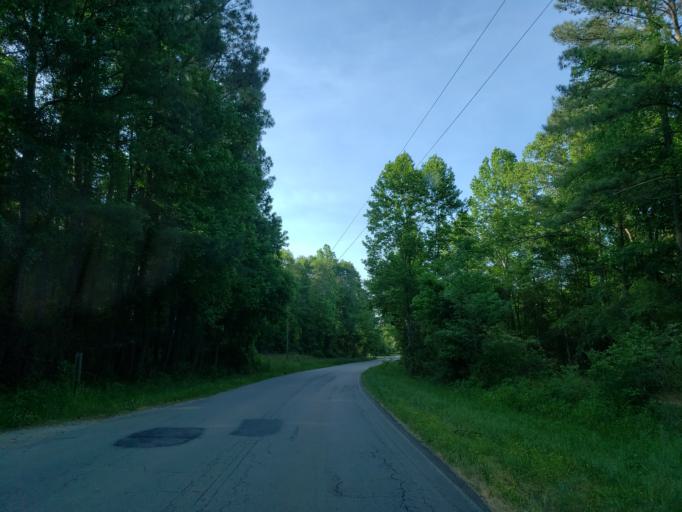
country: US
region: Georgia
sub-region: Carroll County
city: Bowdon
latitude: 33.4779
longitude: -85.3029
